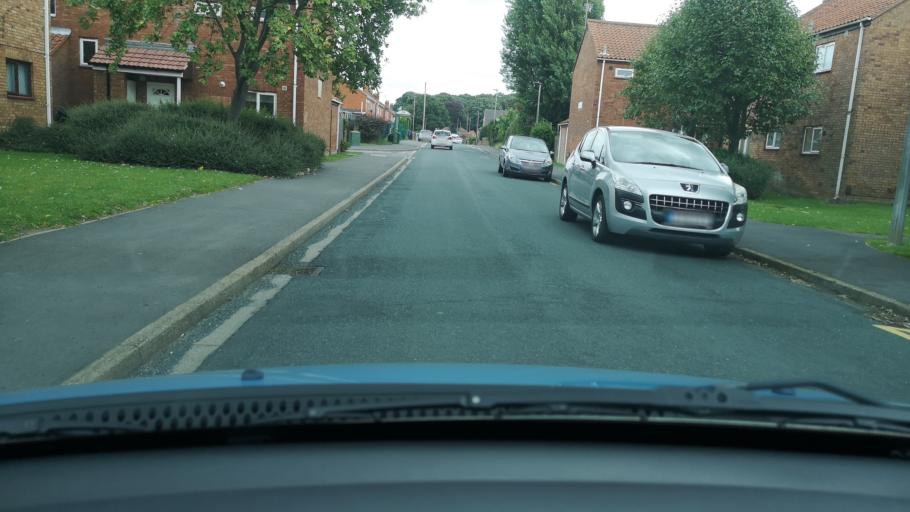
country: GB
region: England
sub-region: North Lincolnshire
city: Scunthorpe
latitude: 53.5890
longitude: -0.6876
